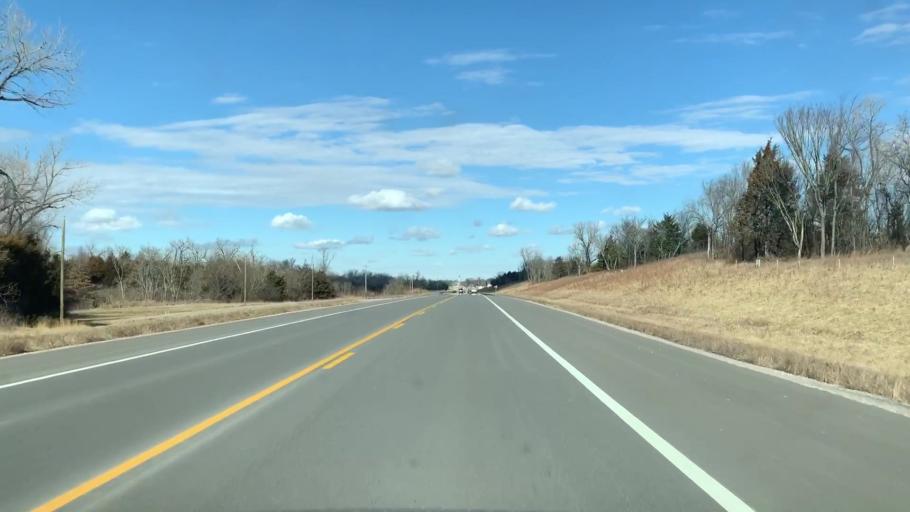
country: US
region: Kansas
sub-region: Crawford County
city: Pittsburg
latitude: 37.3258
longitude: -94.8322
